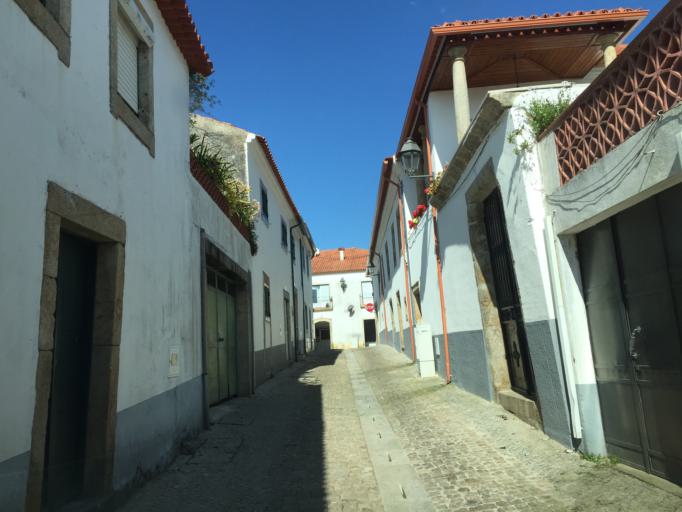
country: PT
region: Leiria
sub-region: Pedrogao Grande
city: Pedrogao Grande
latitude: 39.9157
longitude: -8.1458
